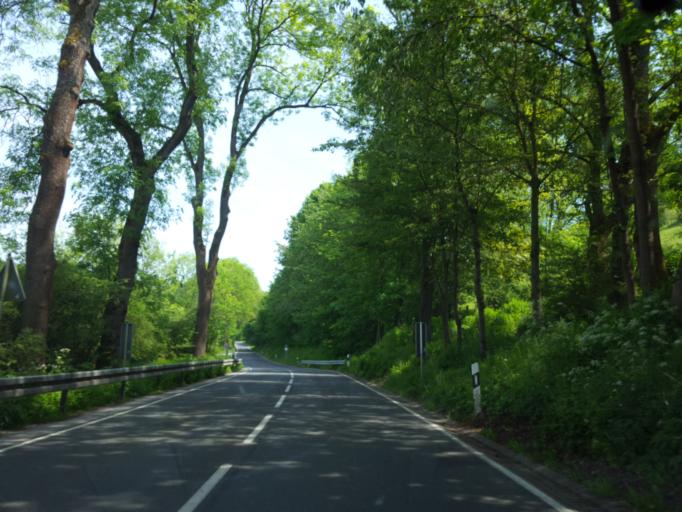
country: DE
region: North Rhine-Westphalia
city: Marsberg
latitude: 51.4379
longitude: 8.8384
